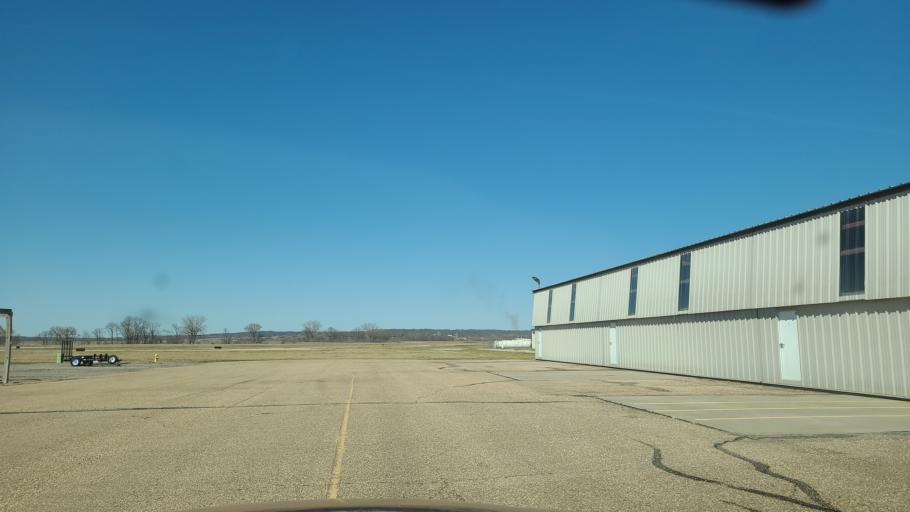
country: US
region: Kansas
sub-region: Douglas County
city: Lawrence
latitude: 39.0039
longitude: -95.2189
